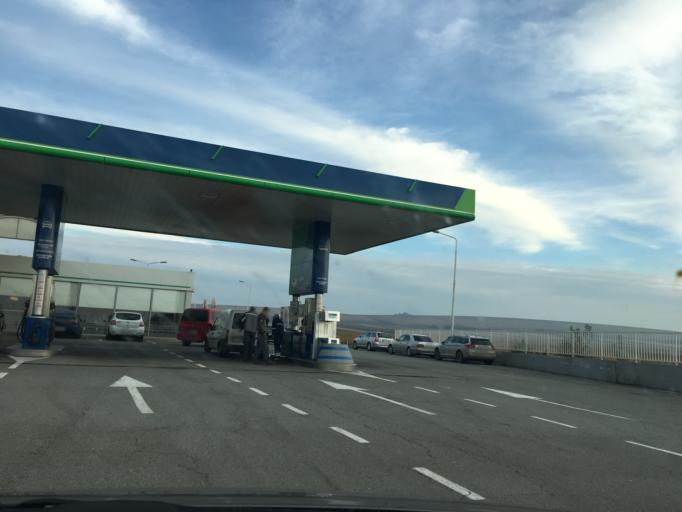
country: RS
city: Beska
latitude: 45.1461
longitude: 20.0847
